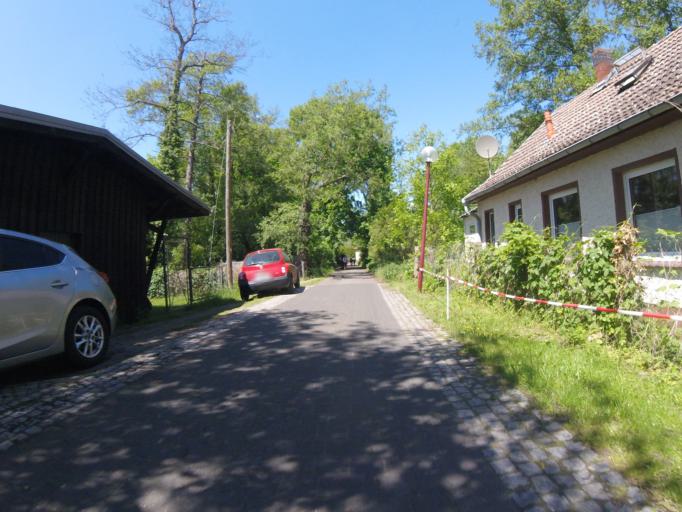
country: DE
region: Brandenburg
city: Teupitz
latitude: 52.1377
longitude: 13.6070
